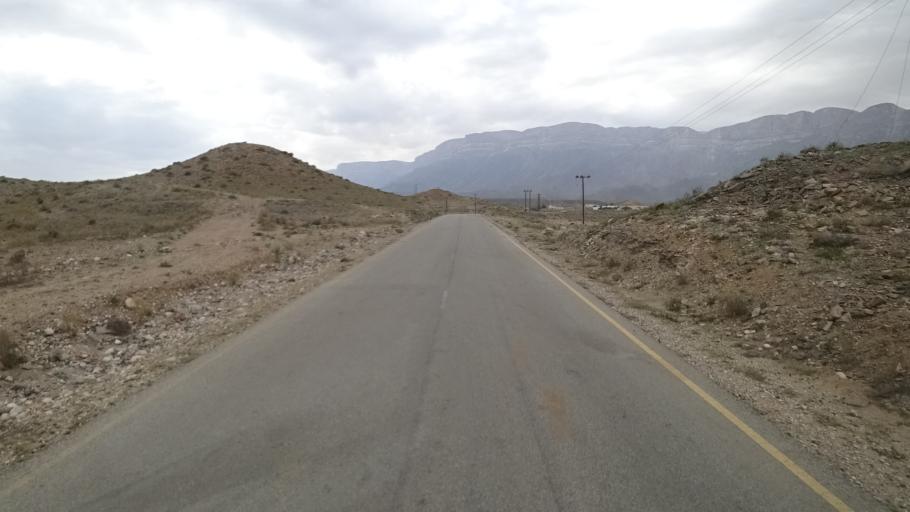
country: OM
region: Zufar
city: Salalah
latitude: 17.1618
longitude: 54.9901
